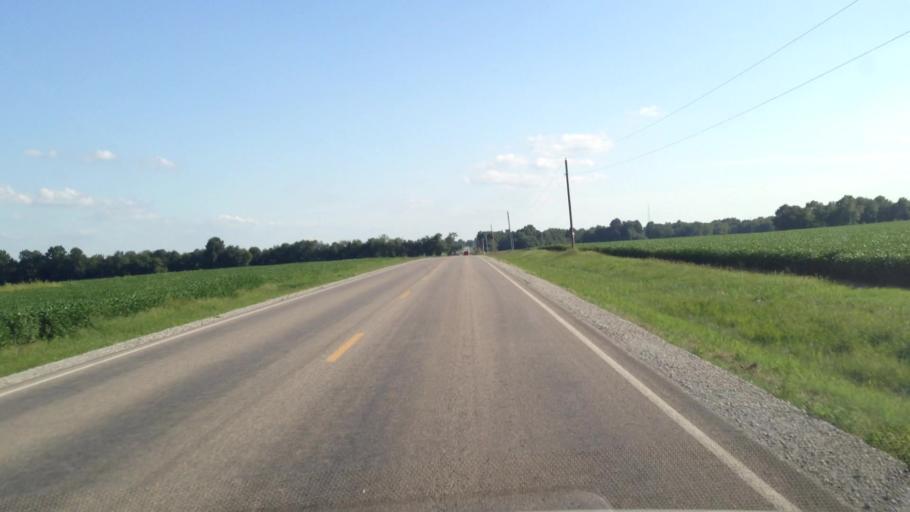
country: US
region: Kansas
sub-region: Crawford County
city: Pittsburg
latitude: 37.3580
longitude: -94.6315
